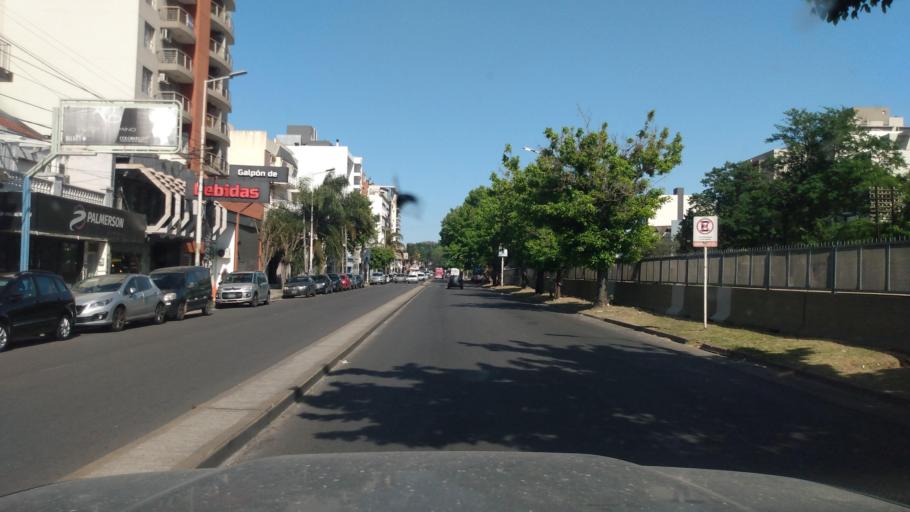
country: AR
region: Buenos Aires
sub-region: Partido de Moron
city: Moron
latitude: -34.6440
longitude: -58.5862
